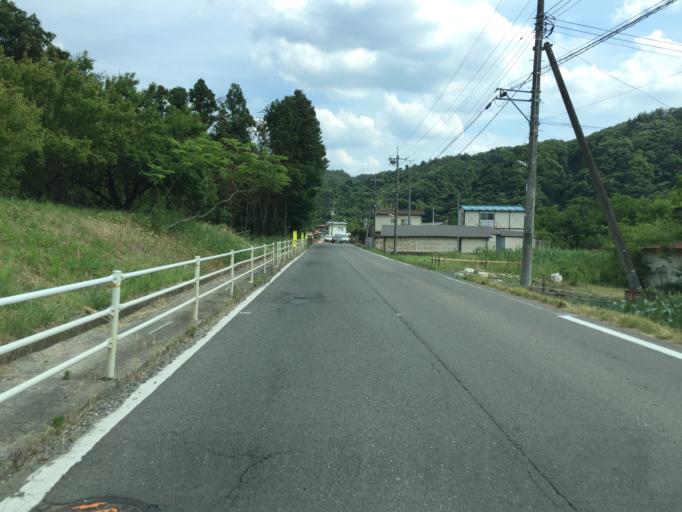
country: JP
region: Fukushima
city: Fukushima-shi
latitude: 37.7207
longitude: 140.4731
